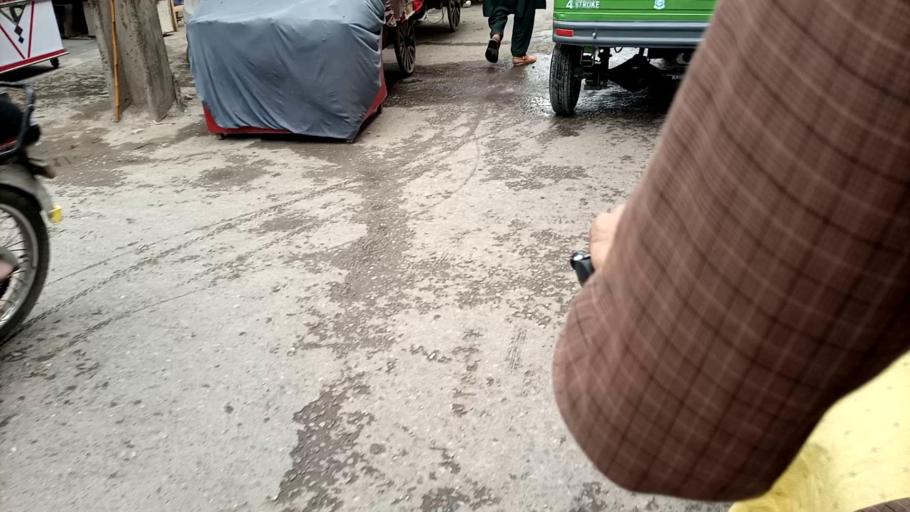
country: PK
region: Khyber Pakhtunkhwa
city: Peshawar
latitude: 34.0167
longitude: 71.5802
